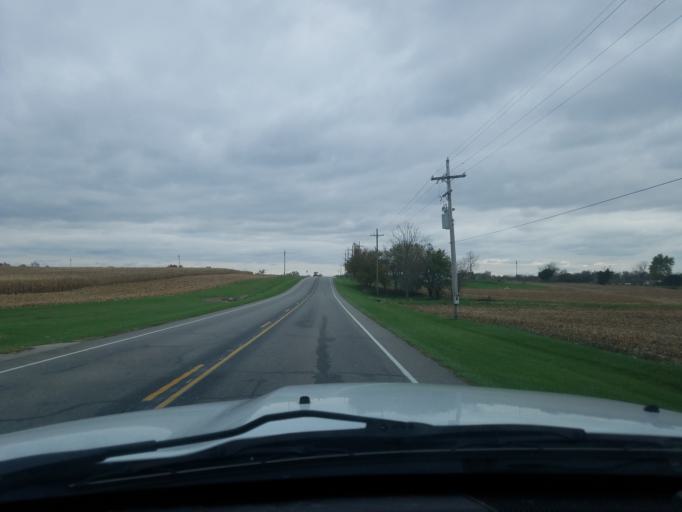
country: US
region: Indiana
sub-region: Bartholomew County
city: Hope
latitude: 39.3230
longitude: -85.7713
